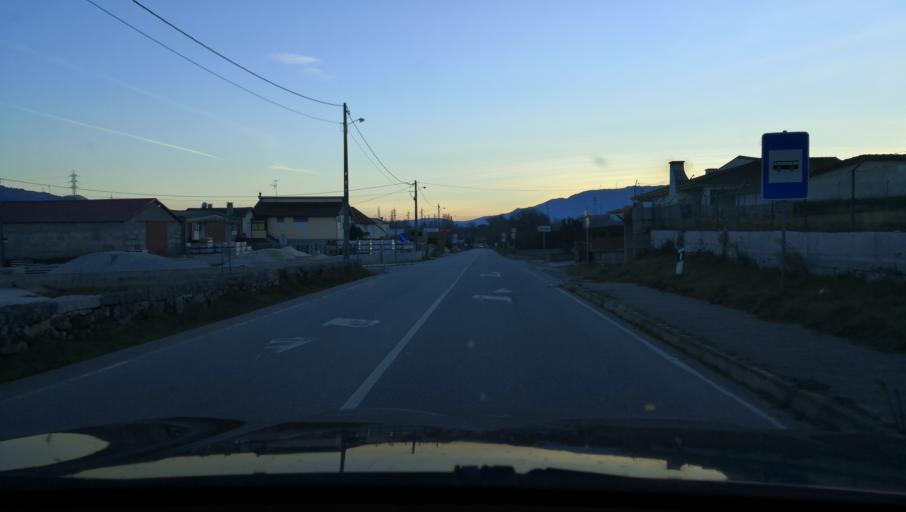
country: PT
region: Vila Real
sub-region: Vila Pouca de Aguiar
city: Vila Pouca de Aguiar
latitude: 41.4703
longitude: -7.6628
